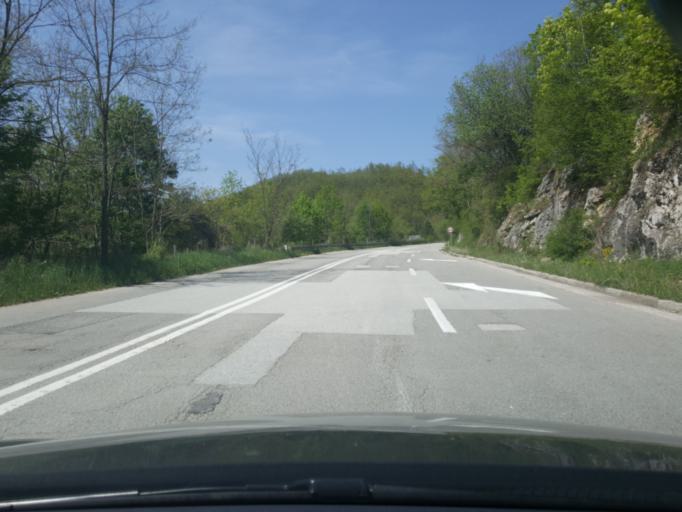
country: RS
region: Central Serbia
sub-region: Zlatiborski Okrug
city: Cajetina
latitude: 43.8062
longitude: 19.6465
